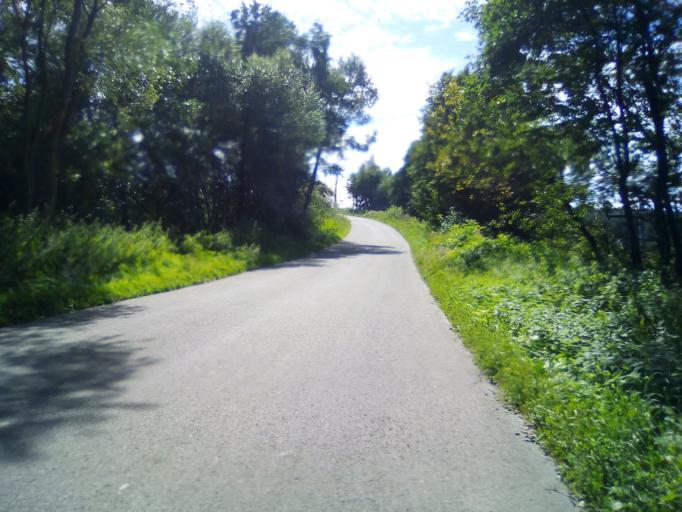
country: PL
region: Subcarpathian Voivodeship
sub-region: Powiat strzyzowski
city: Konieczkowa
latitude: 49.8274
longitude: 21.9277
